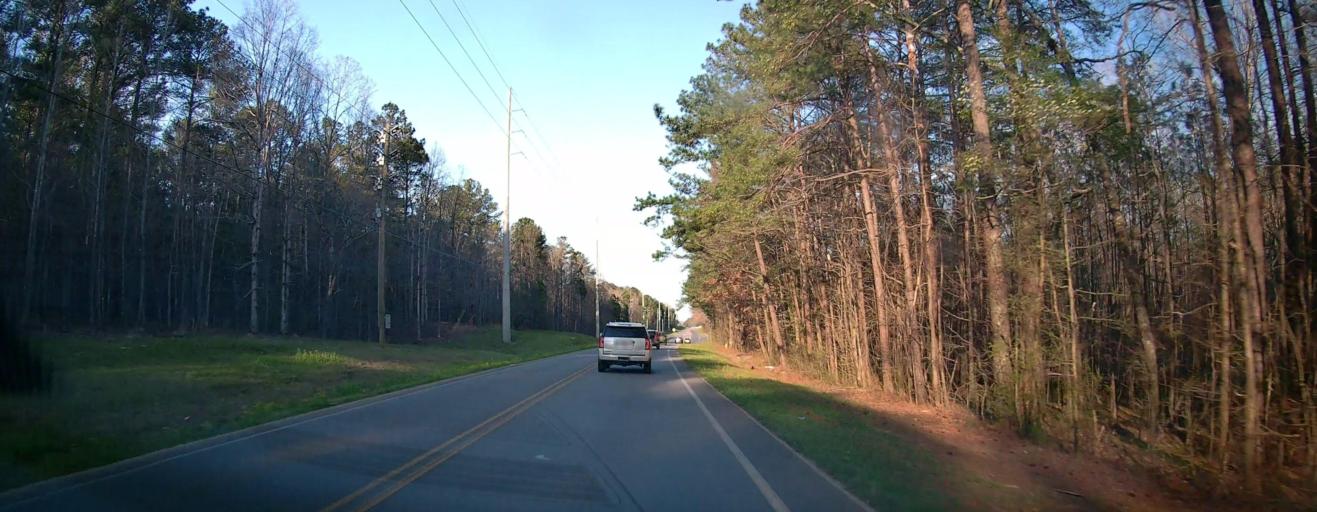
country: US
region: Alabama
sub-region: Shelby County
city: Indian Springs Village
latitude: 33.3145
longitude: -86.7279
